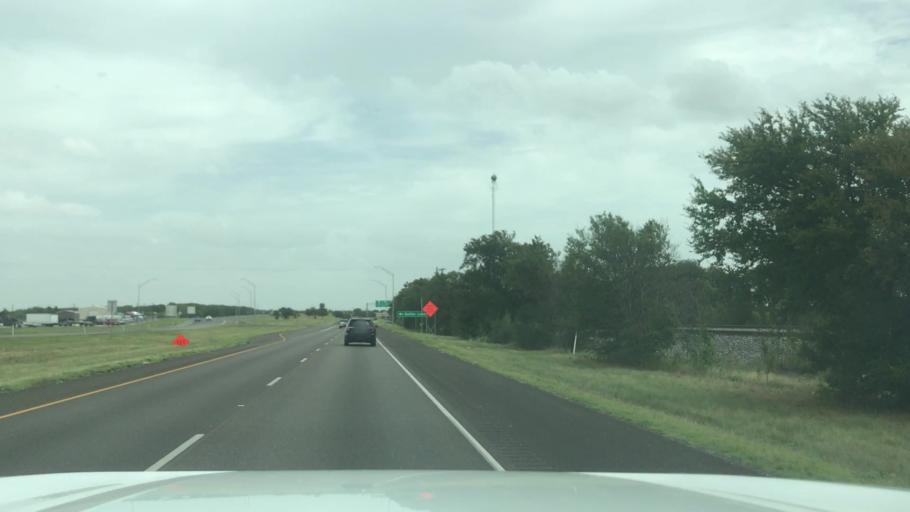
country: US
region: Texas
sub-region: McLennan County
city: Riesel
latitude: 31.5174
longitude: -96.9661
